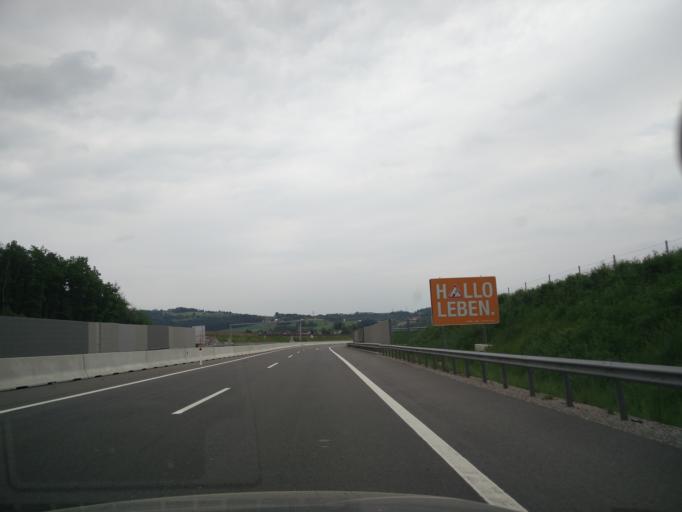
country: AT
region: Upper Austria
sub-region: Politischer Bezirk Urfahr-Umgebung
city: Engerwitzdorf
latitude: 48.3678
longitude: 14.4802
